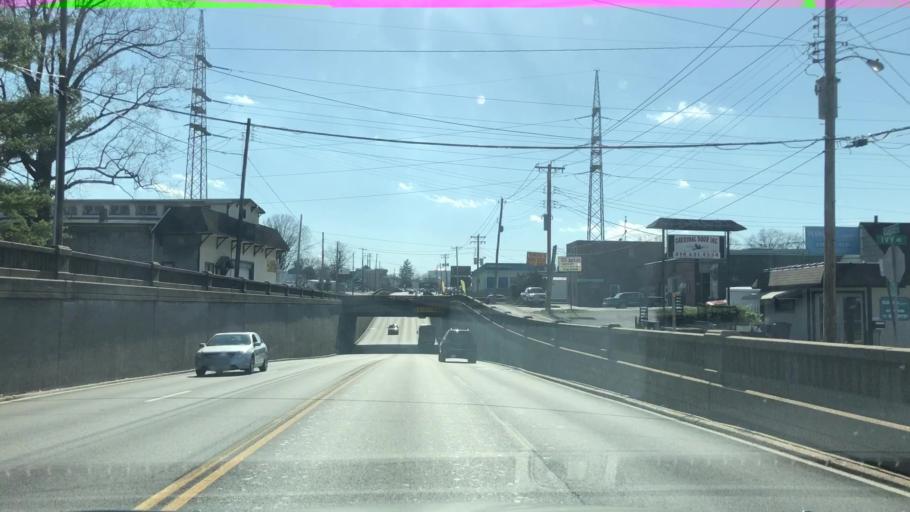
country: US
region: Missouri
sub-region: Saint Louis County
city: Affton
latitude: 38.5521
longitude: -90.3257
